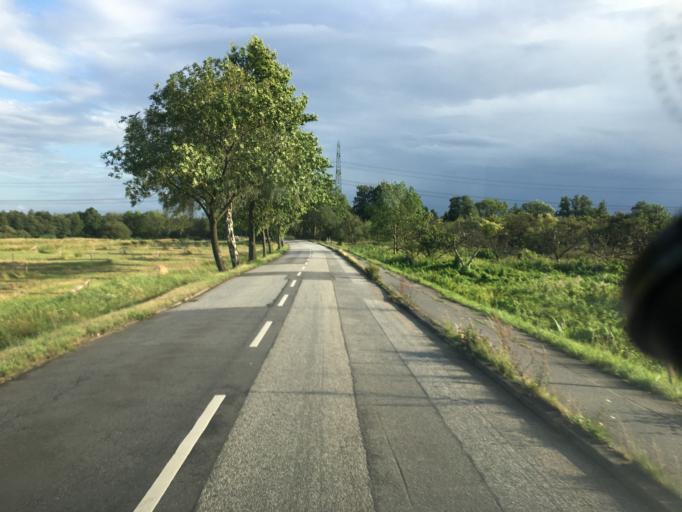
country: DE
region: Lower Saxony
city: Neu Wulmstorf
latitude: 53.4952
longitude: 9.8742
